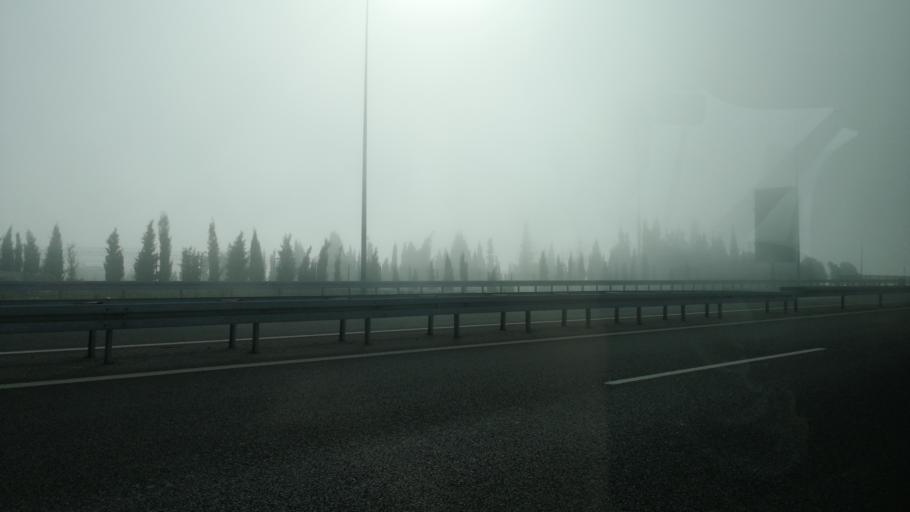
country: TR
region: Kocaeli
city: Tavsanli
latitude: 40.7709
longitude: 29.5182
